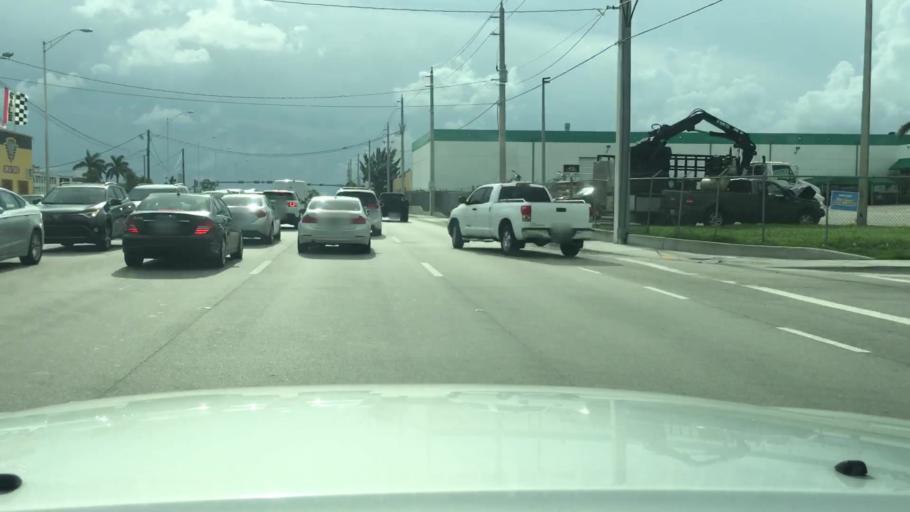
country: US
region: Florida
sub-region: Miami-Dade County
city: Hialeah Gardens
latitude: 25.8408
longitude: -80.3317
